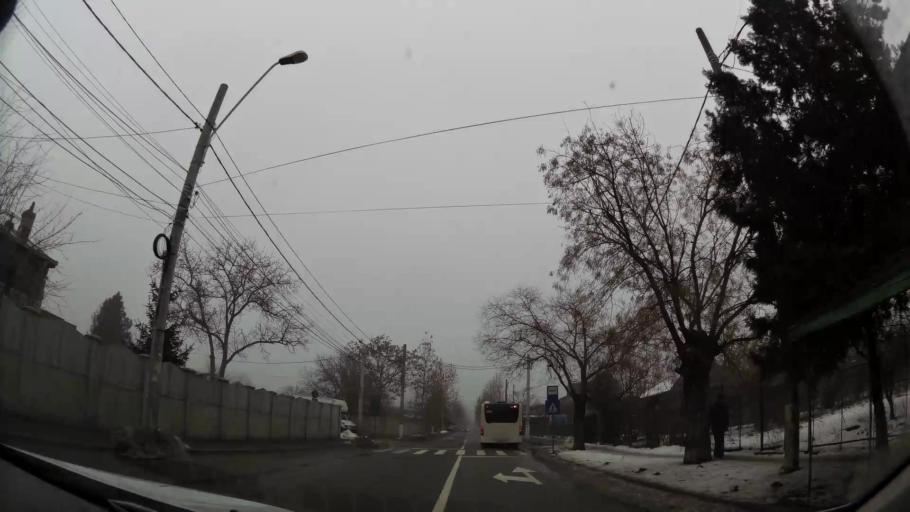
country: RO
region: Ilfov
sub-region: Comuna Chiajna
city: Rosu
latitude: 44.4673
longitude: 26.0157
